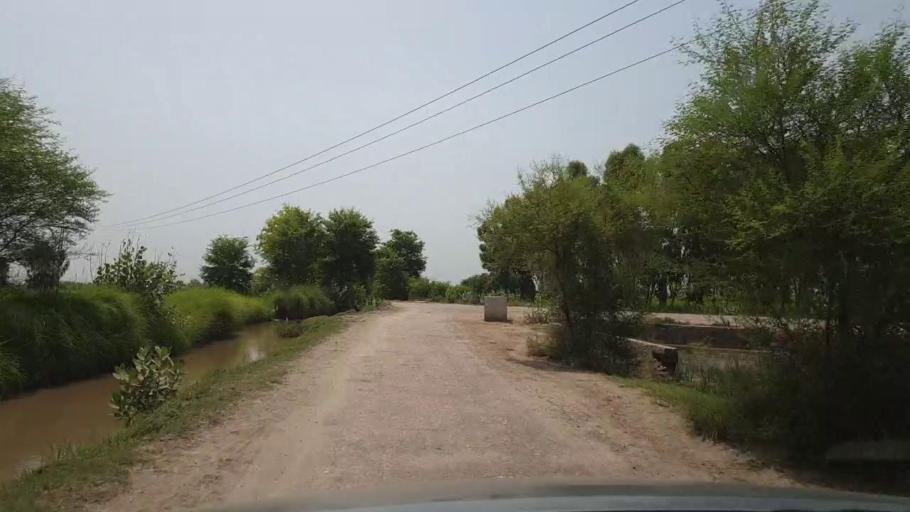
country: PK
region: Sindh
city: Madeji
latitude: 27.7730
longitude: 68.4322
